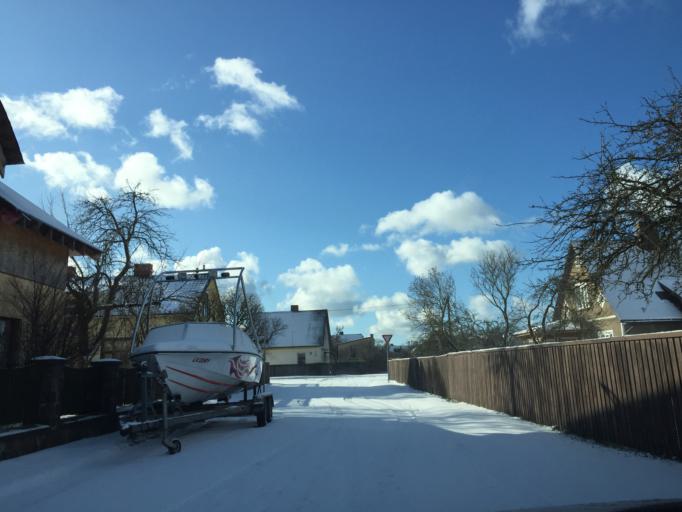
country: LV
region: Ventspils
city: Ventspils
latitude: 57.3845
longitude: 21.5580
